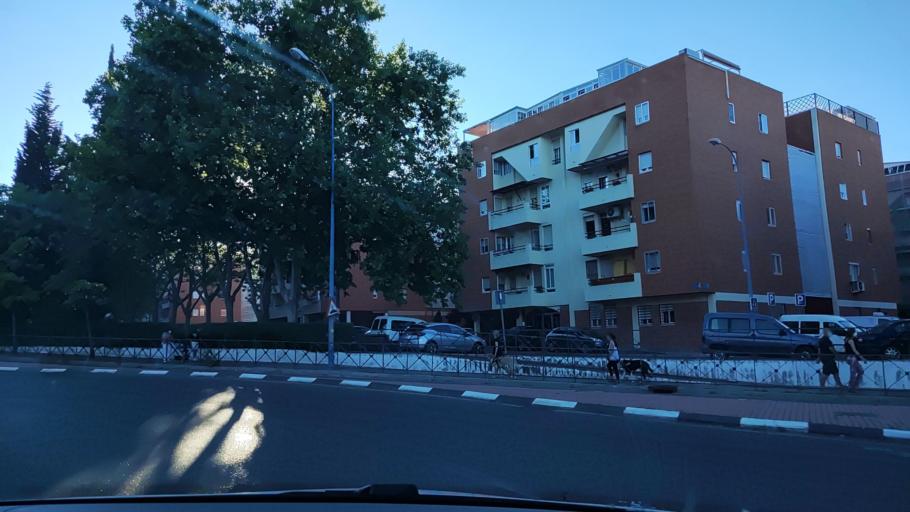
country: ES
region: Madrid
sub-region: Provincia de Madrid
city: Leganes
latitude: 40.3349
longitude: -3.7602
